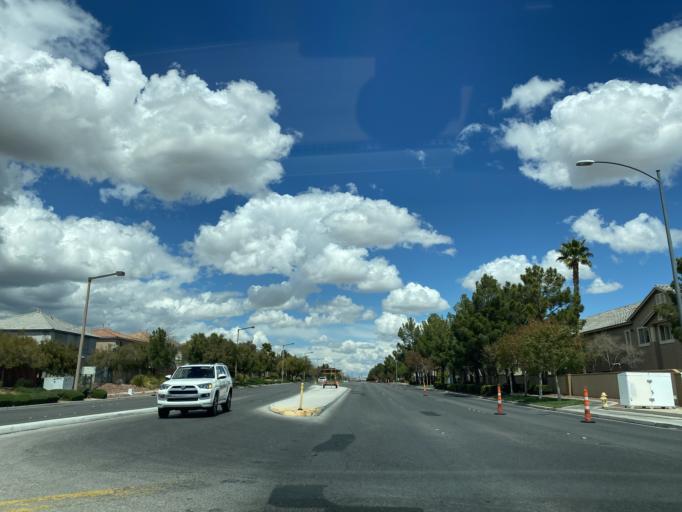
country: US
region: Nevada
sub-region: Clark County
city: Summerlin South
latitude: 36.1461
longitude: -115.3155
